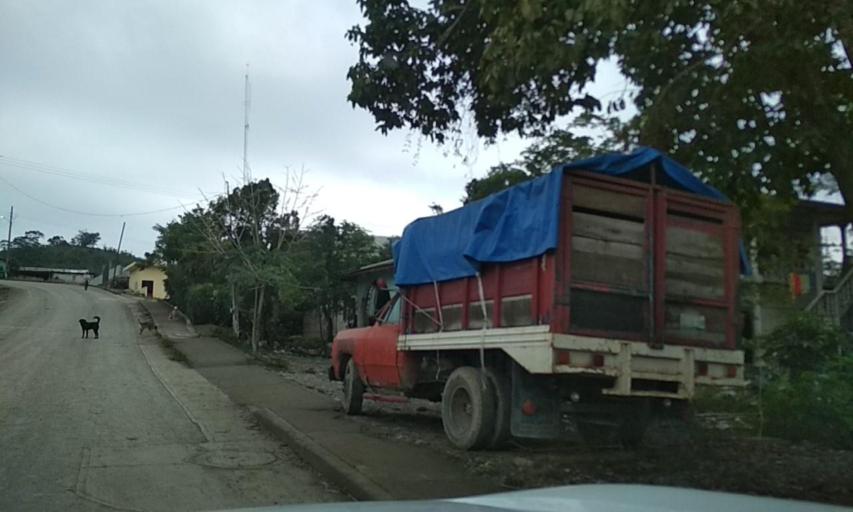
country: MX
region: Veracruz
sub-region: Coatzintla
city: Manuel Maria Contreras
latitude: 20.3598
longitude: -97.5116
